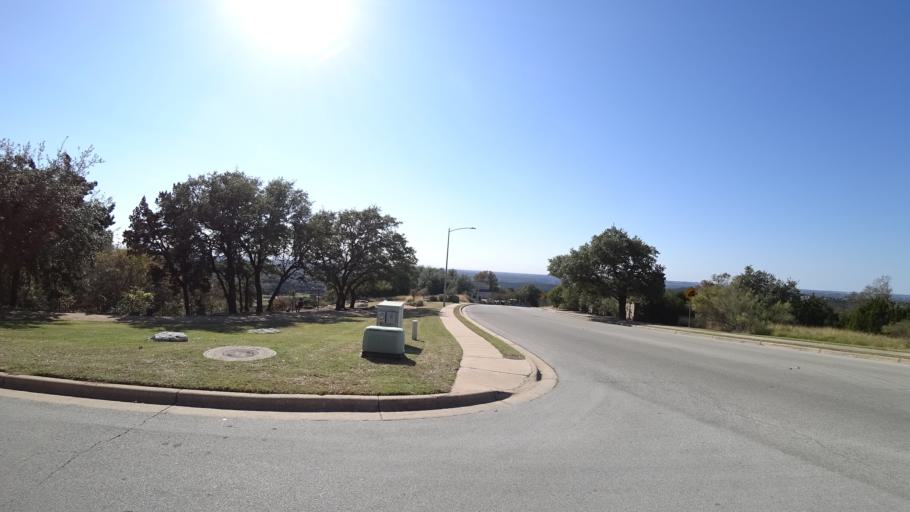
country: US
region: Texas
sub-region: Travis County
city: Lost Creek
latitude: 30.3761
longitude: -97.8532
